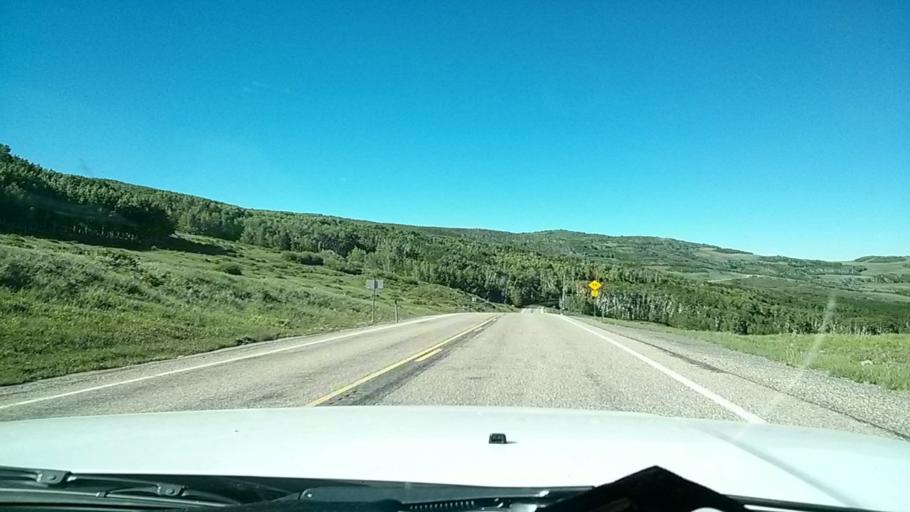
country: US
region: Utah
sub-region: Wayne County
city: Loa
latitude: 38.0146
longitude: -111.3578
